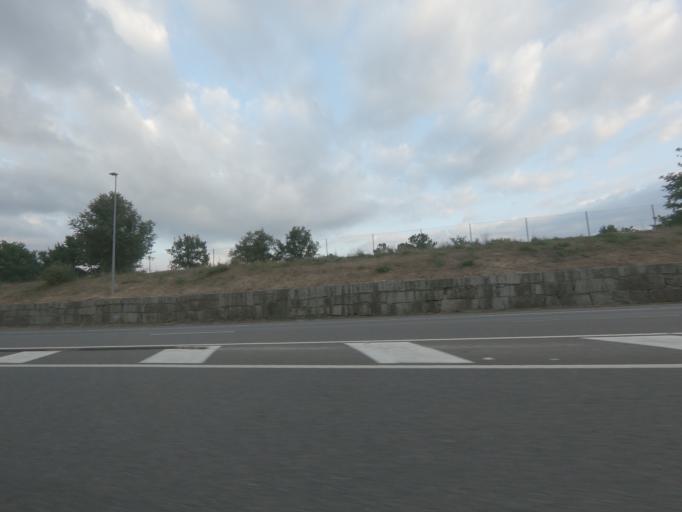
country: ES
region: Galicia
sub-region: Provincia de Ourense
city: Taboadela
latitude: 42.2861
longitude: -7.8307
